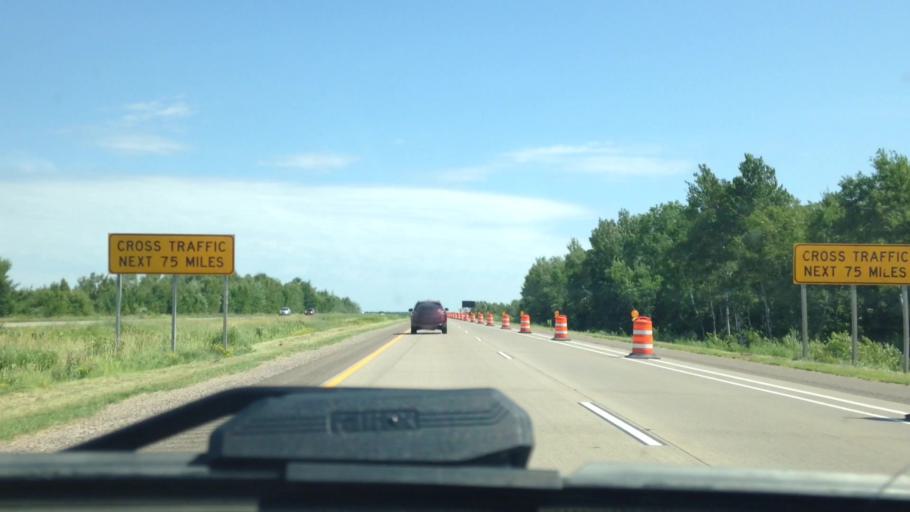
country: US
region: Wisconsin
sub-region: Barron County
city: Rice Lake
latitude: 45.5691
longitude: -91.7634
